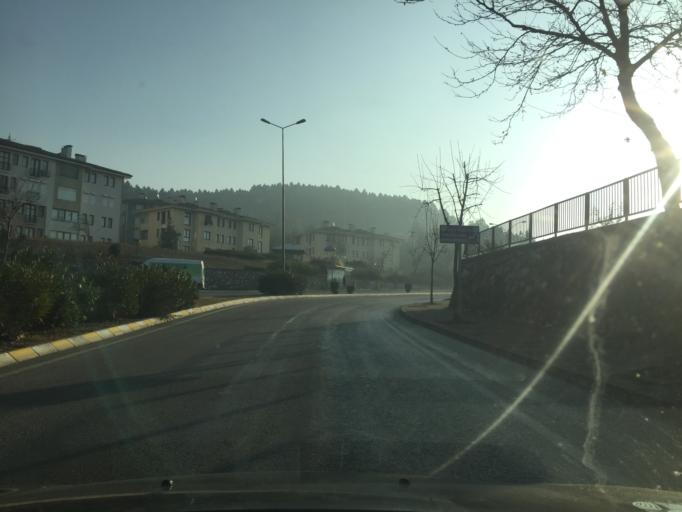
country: TR
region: Duzce
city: Duzce
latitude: 40.8680
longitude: 31.2295
